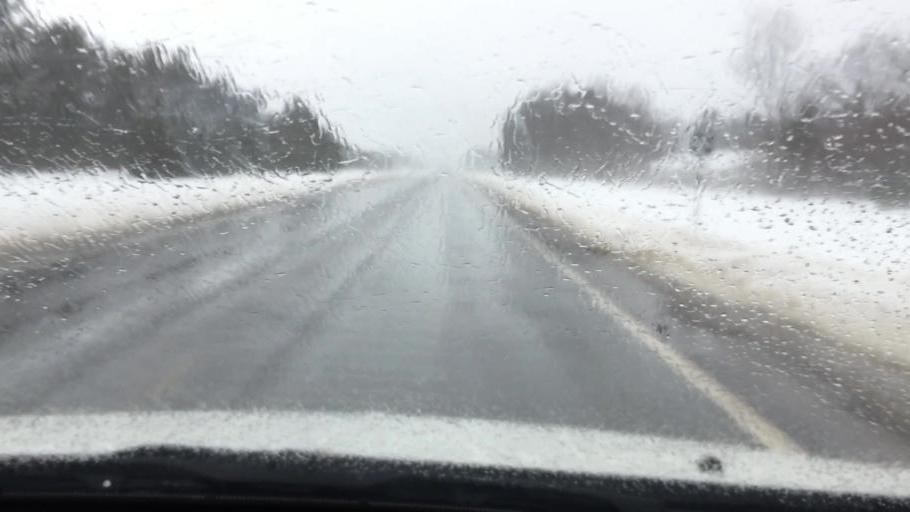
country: US
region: Michigan
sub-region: Antrim County
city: Mancelona
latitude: 44.9308
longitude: -85.0509
